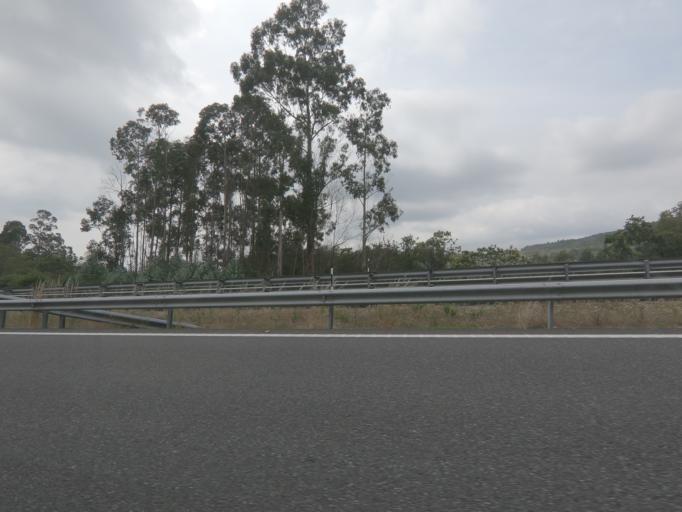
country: ES
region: Galicia
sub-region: Provincia de Pontevedra
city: Covelo
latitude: 42.1687
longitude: -8.3807
